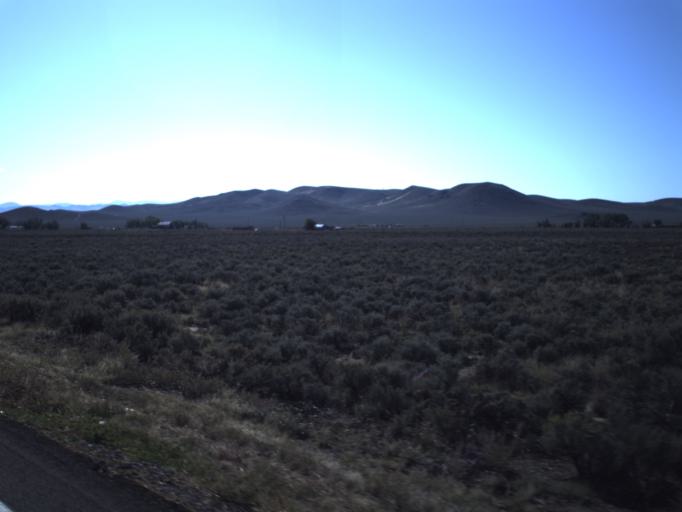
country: US
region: Utah
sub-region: Washington County
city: Enterprise
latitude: 37.7513
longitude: -113.7734
